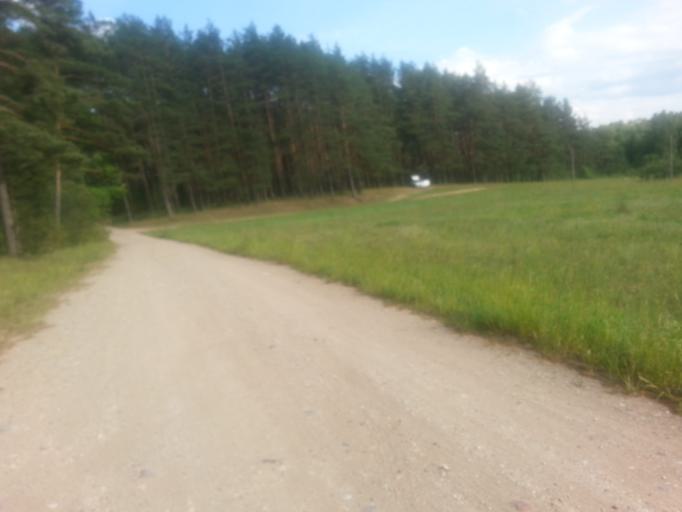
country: BY
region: Minsk
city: Narach
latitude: 54.9695
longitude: 26.6152
